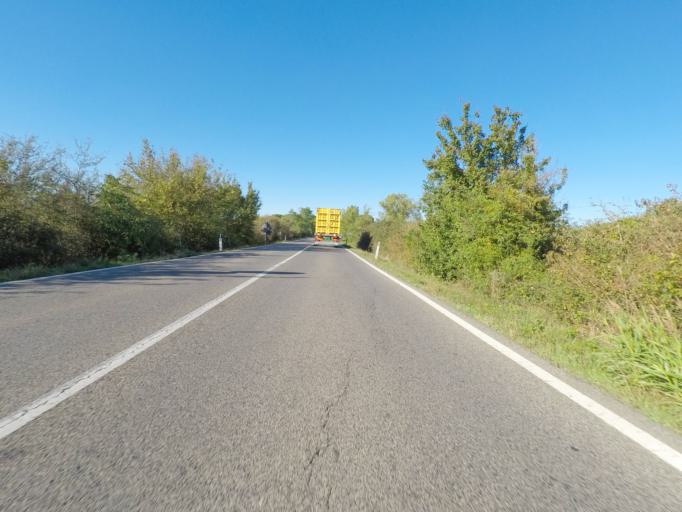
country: IT
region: Tuscany
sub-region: Provincia di Siena
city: Rosia
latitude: 43.1979
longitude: 11.2763
